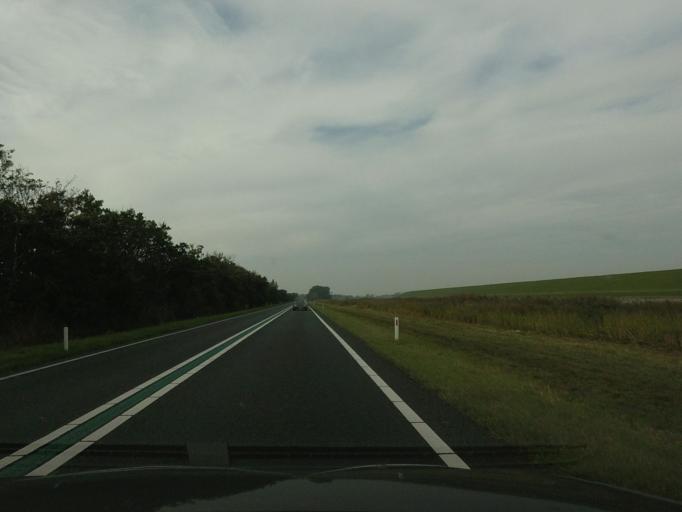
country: NL
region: North Holland
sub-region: Gemeente Den Helder
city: Den Helder
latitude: 52.9068
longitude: 4.8158
